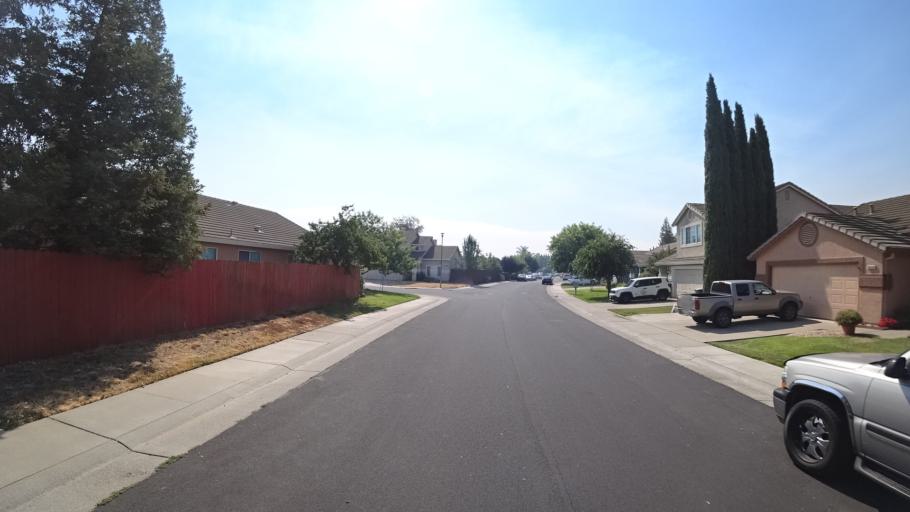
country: US
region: California
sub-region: Sacramento County
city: Laguna
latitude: 38.4263
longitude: -121.4125
